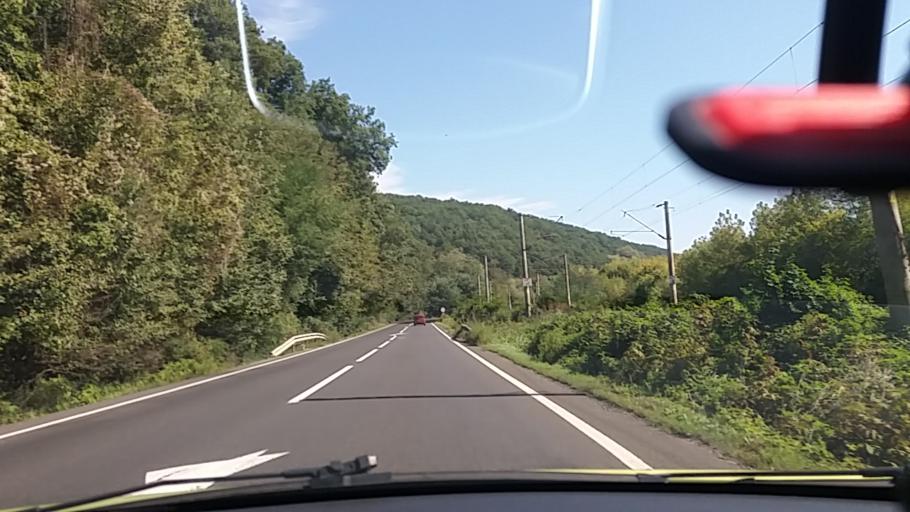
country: RO
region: Arad
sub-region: Comuna Conop
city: Conop
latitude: 46.1014
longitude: 21.9248
